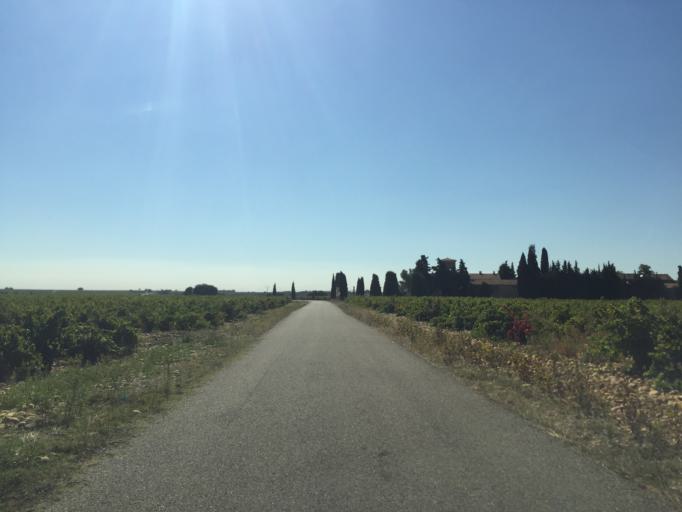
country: FR
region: Provence-Alpes-Cote d'Azur
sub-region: Departement du Vaucluse
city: Chateauneuf-du-Pape
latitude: 44.0830
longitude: 4.8273
